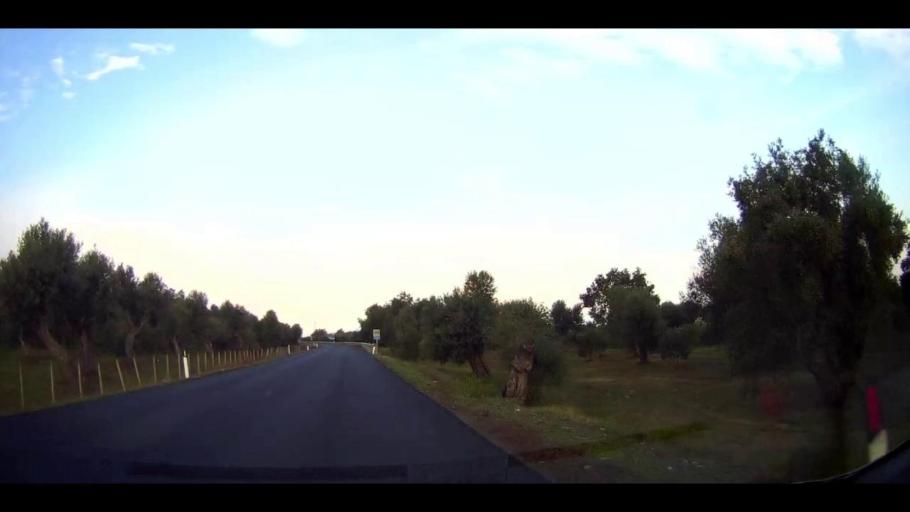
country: IT
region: Calabria
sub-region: Provincia di Crotone
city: Torretta
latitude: 39.4698
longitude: 17.0189
